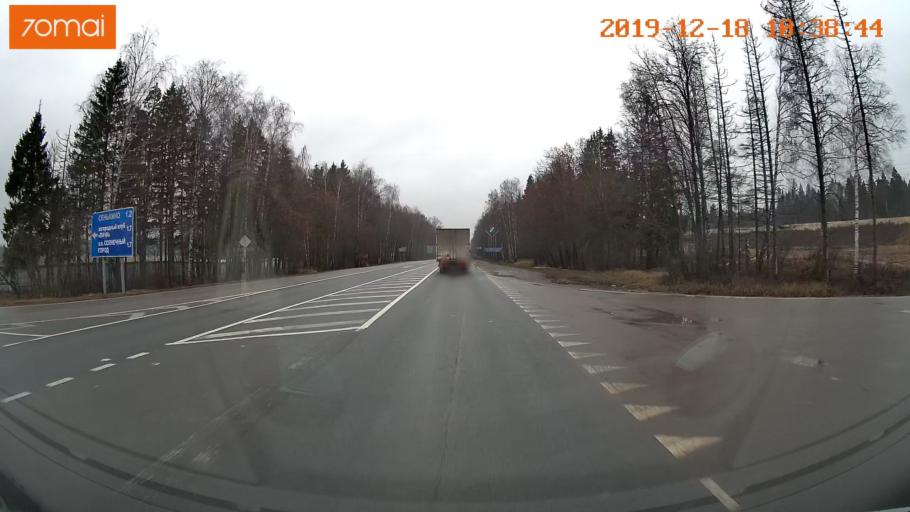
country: RU
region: Moskovskaya
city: Aprelevka
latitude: 55.4380
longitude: 37.1514
